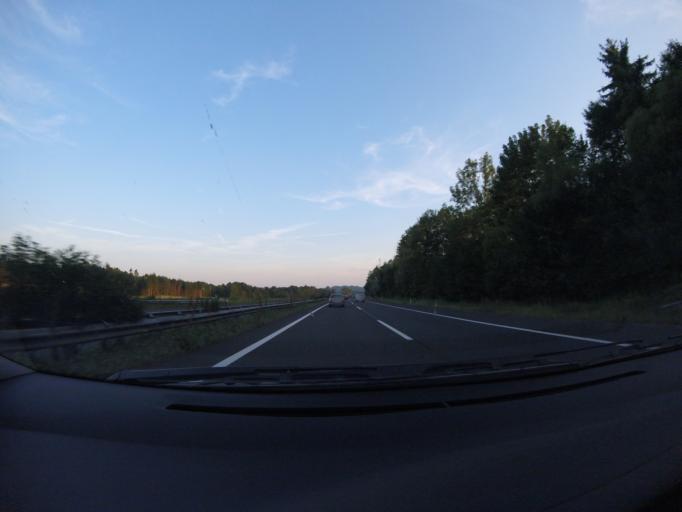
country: AT
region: Styria
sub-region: Politischer Bezirk Hartberg-Fuerstenfeld
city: Hainersdorf
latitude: 47.1010
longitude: 15.9842
